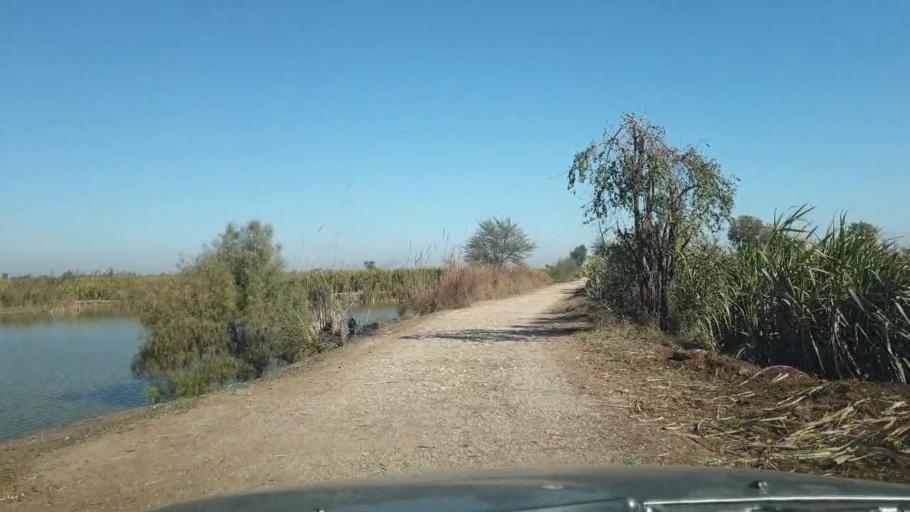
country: PK
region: Sindh
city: Ghotki
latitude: 28.0203
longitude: 69.2830
